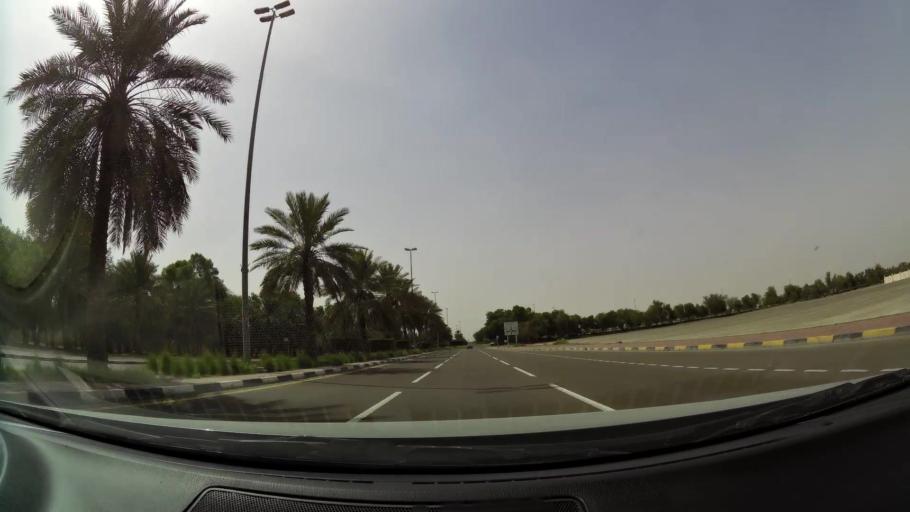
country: AE
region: Abu Dhabi
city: Al Ain
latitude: 24.1835
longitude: 55.6603
